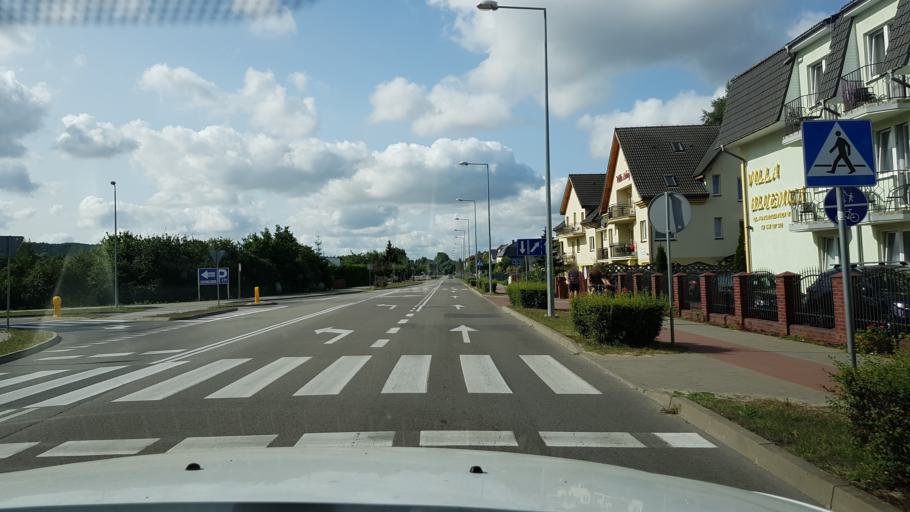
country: PL
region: West Pomeranian Voivodeship
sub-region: Powiat kamienski
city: Miedzyzdroje
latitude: 53.9262
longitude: 14.4436
